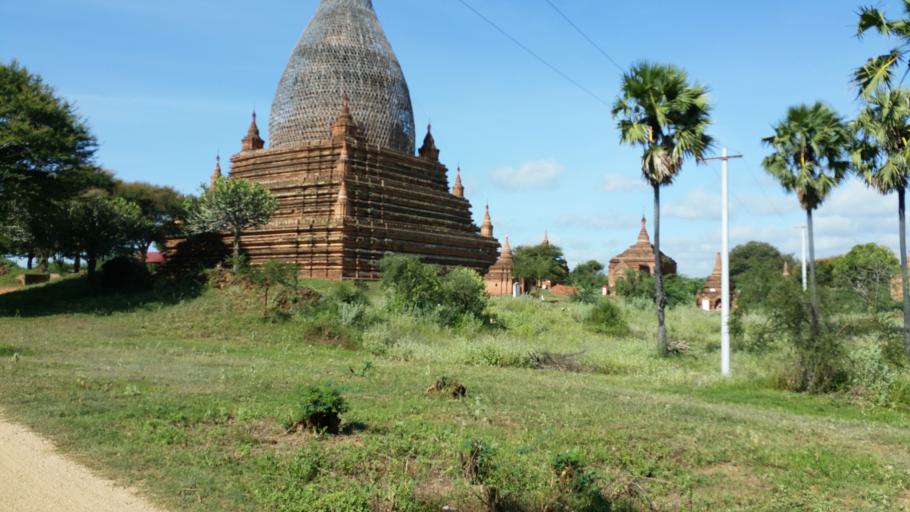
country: MM
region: Magway
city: Chauk
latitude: 21.1475
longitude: 94.8581
